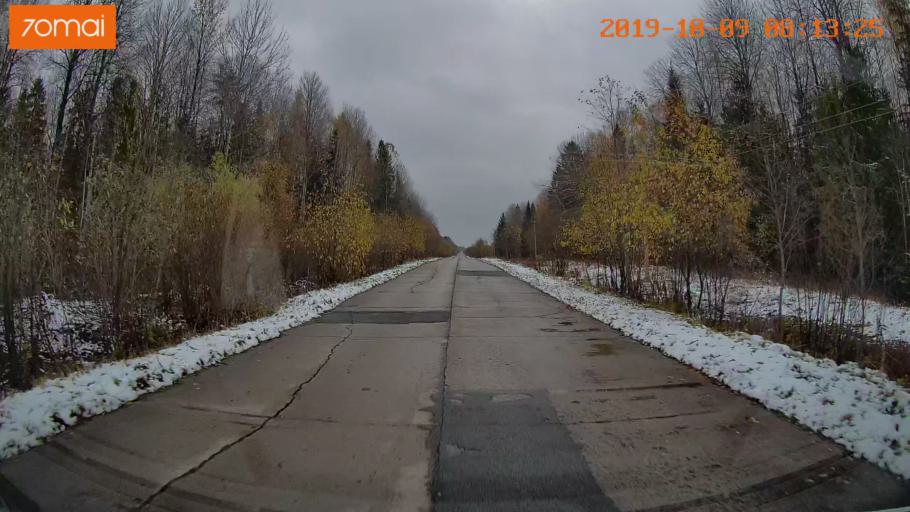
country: RU
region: Vologda
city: Gryazovets
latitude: 58.7234
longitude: 40.1395
